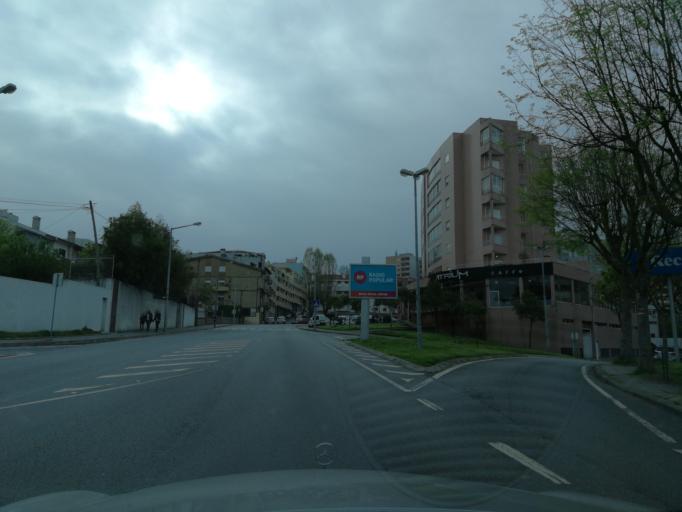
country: PT
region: Braga
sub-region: Braga
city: Braga
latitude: 41.5538
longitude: -8.4376
